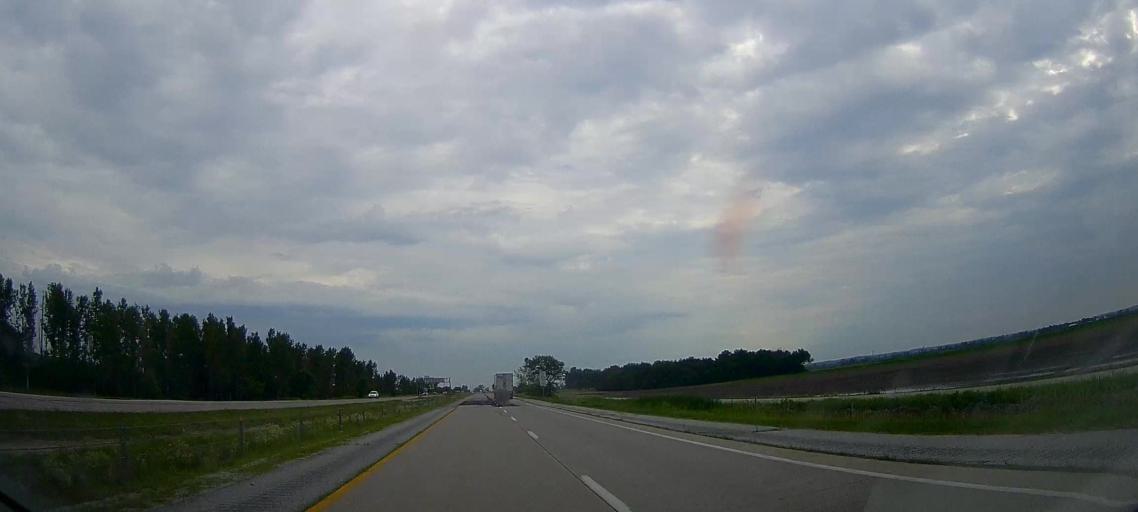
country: US
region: Iowa
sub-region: Harrison County
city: Missouri Valley
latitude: 41.4818
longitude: -95.9004
